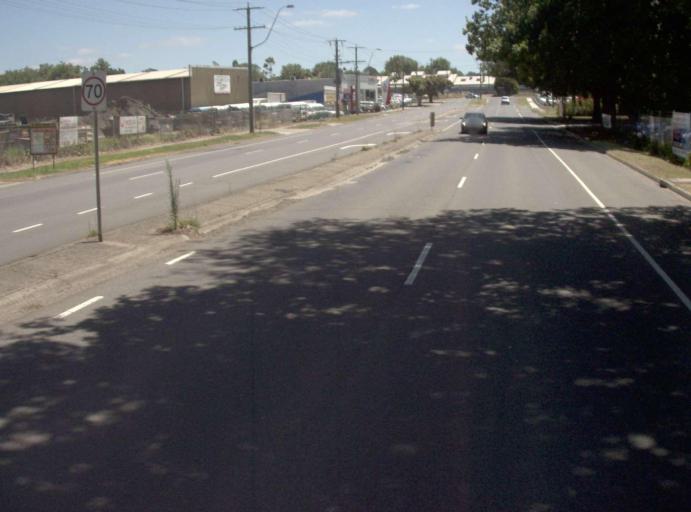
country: AU
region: Victoria
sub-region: Baw Baw
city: Warragul
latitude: -38.1680
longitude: 145.9323
